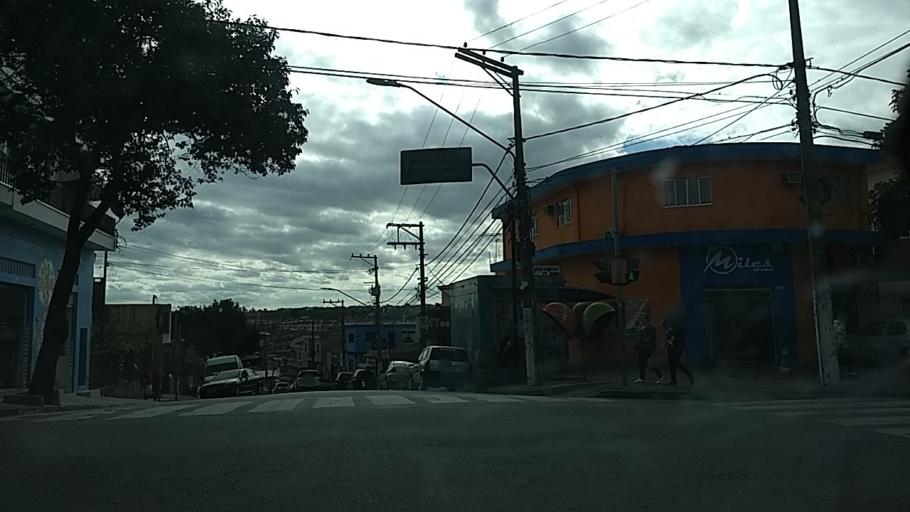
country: BR
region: Sao Paulo
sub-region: Osasco
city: Osasco
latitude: -23.5128
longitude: -46.7785
